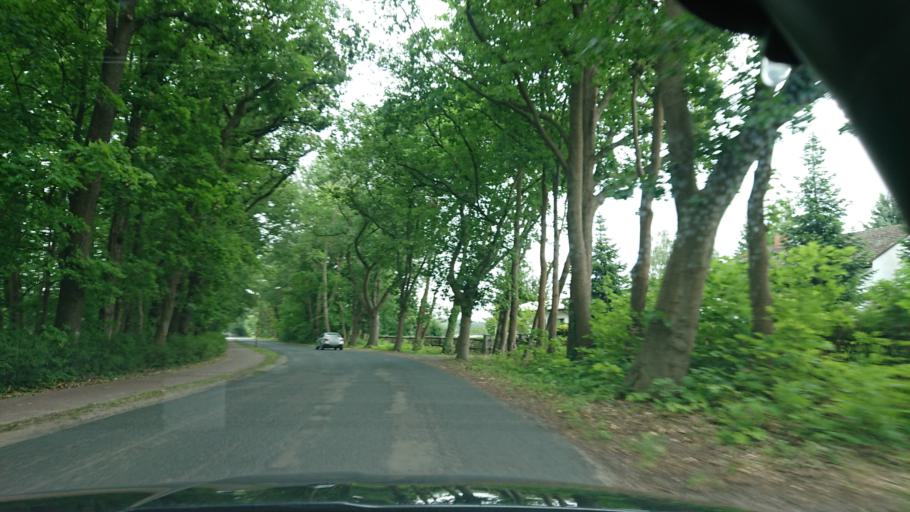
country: DE
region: Brandenburg
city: Kyritz
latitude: 52.9395
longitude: 12.4148
